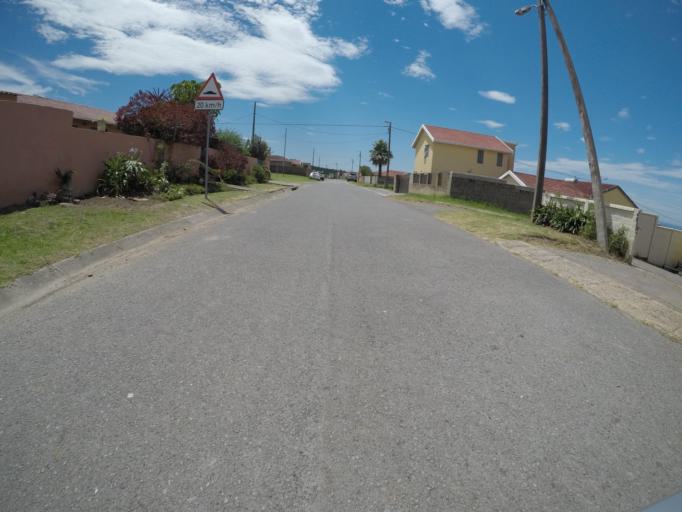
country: ZA
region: Eastern Cape
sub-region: Buffalo City Metropolitan Municipality
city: East London
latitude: -33.0428
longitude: 27.8651
